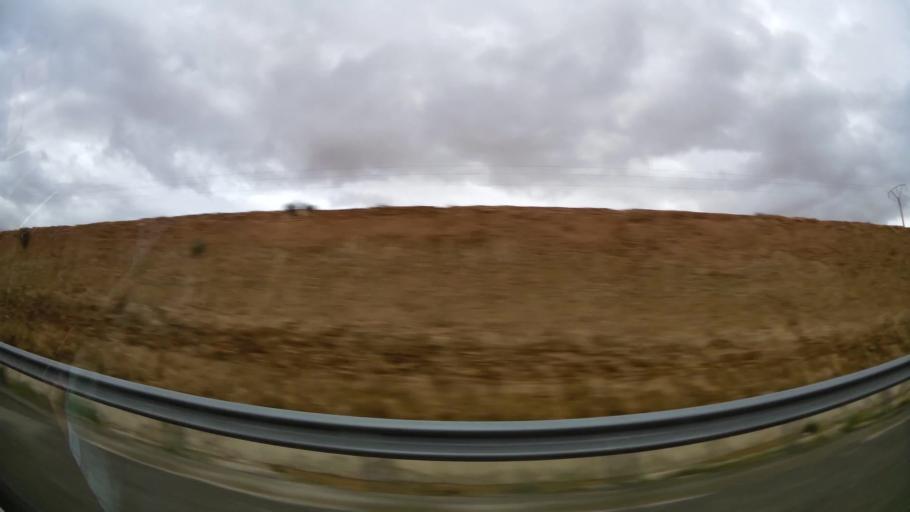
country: MA
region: Taza-Al Hoceima-Taounate
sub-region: Taza
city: Guercif
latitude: 34.3049
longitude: -3.6820
